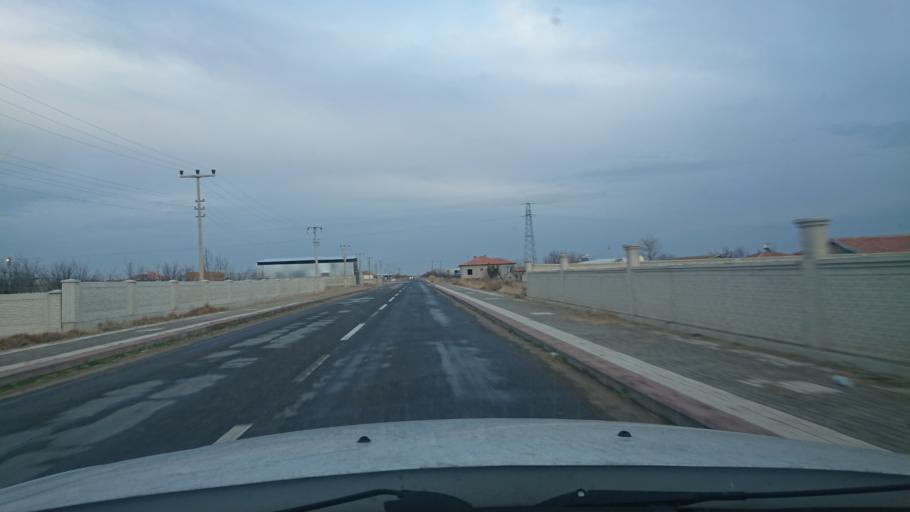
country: TR
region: Aksaray
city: Yesilova
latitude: 38.2951
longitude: 33.7590
